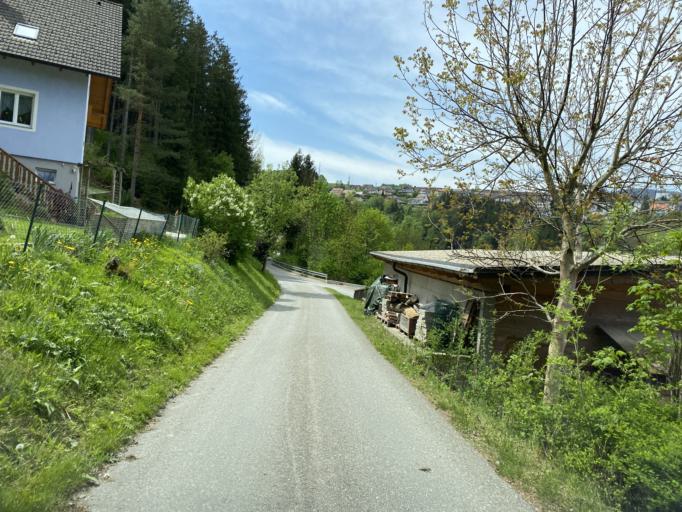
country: AT
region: Styria
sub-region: Politischer Bezirk Weiz
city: Birkfeld
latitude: 47.3516
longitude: 15.7016
